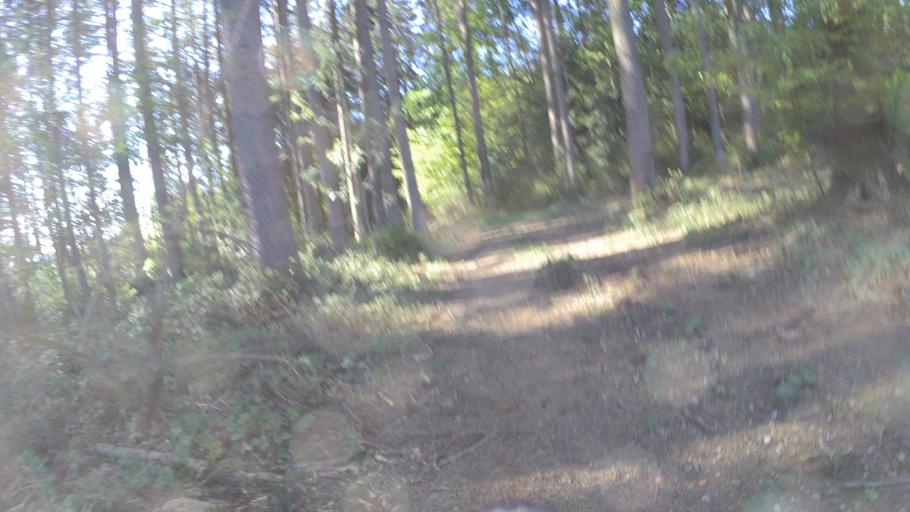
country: DE
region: Bavaria
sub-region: Upper Bavaria
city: Traunreut
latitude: 47.9363
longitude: 12.5677
